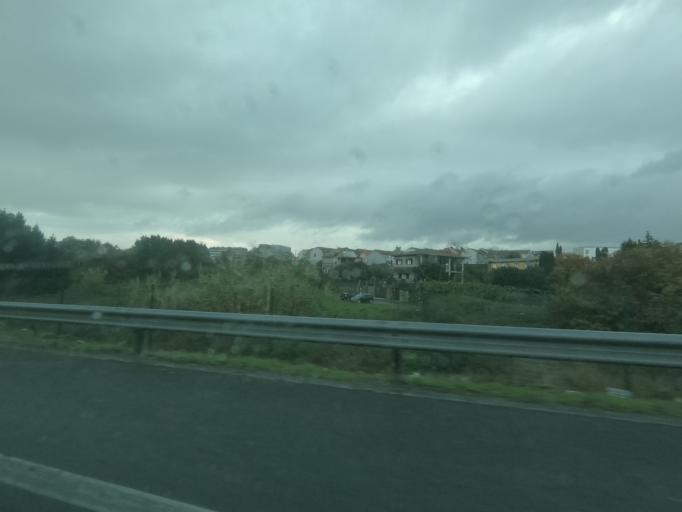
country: ES
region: Galicia
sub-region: Provincia de Pontevedra
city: Pontevedra
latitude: 42.4217
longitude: -8.6505
